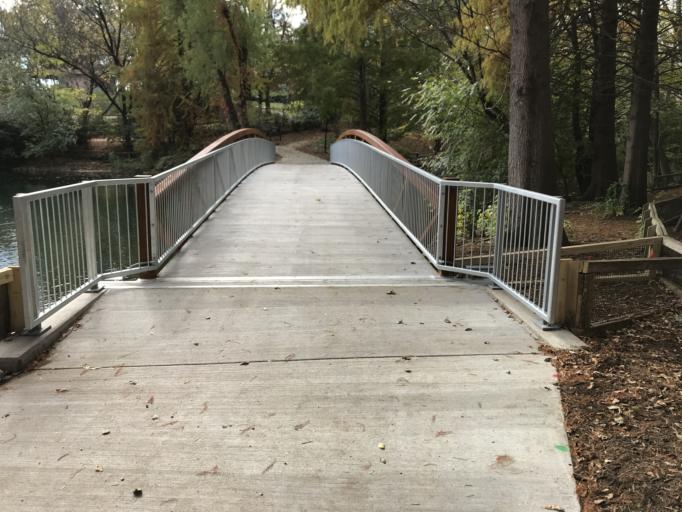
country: US
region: Kentucky
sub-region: Jefferson County
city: Audubon Park
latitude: 38.2044
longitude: -85.7067
